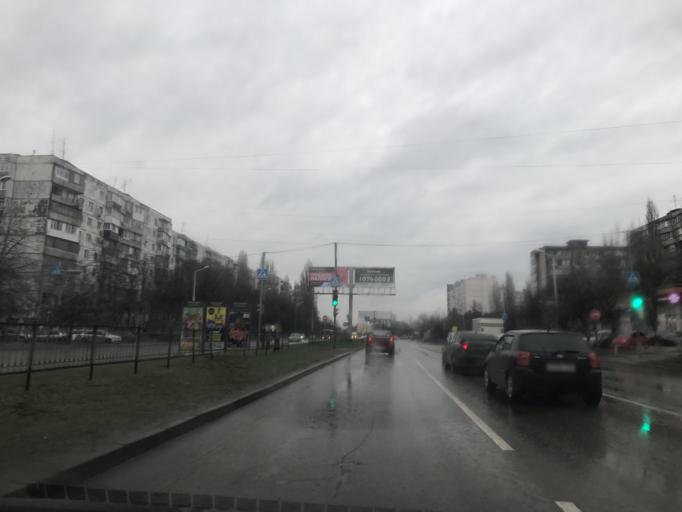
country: RU
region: Rostov
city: Severnyy
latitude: 47.2966
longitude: 39.7132
